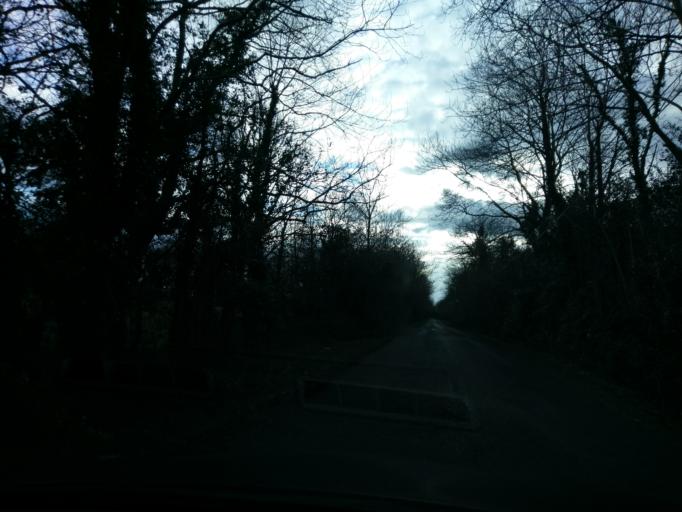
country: IE
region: Connaught
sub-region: County Galway
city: Athenry
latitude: 53.3576
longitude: -8.6504
